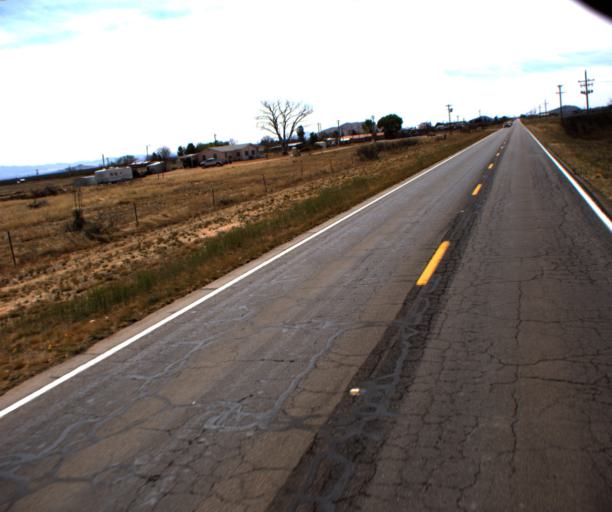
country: US
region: Arizona
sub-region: Cochise County
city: Willcox
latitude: 31.9653
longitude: -109.8435
